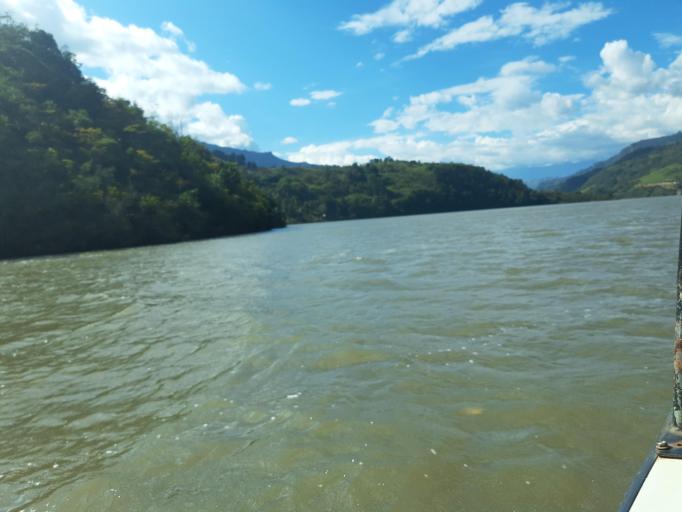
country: CO
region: Boyaca
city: Chivor
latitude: 4.9382
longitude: -73.3148
